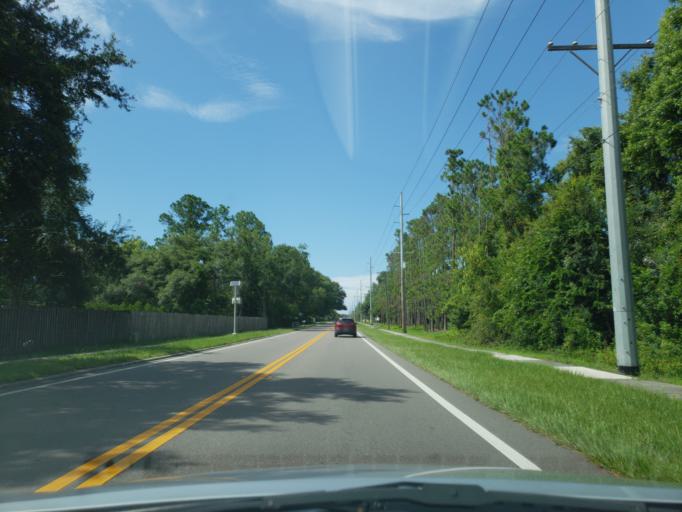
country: US
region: Florida
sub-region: Hillsborough County
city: Carrollwood Village
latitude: 28.0724
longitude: -82.5417
